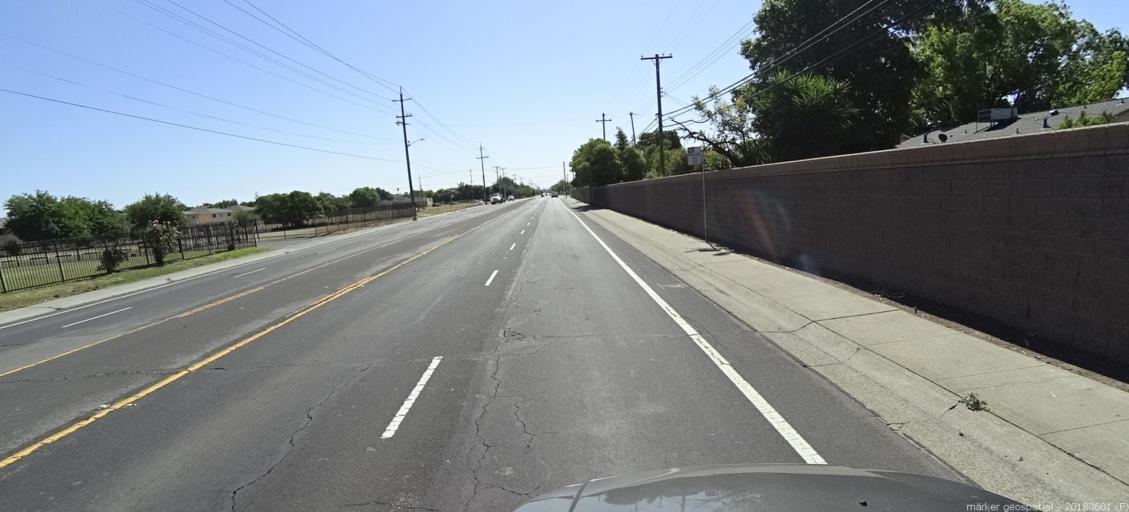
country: US
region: California
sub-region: Sacramento County
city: Parkway
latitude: 38.4814
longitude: -121.4837
